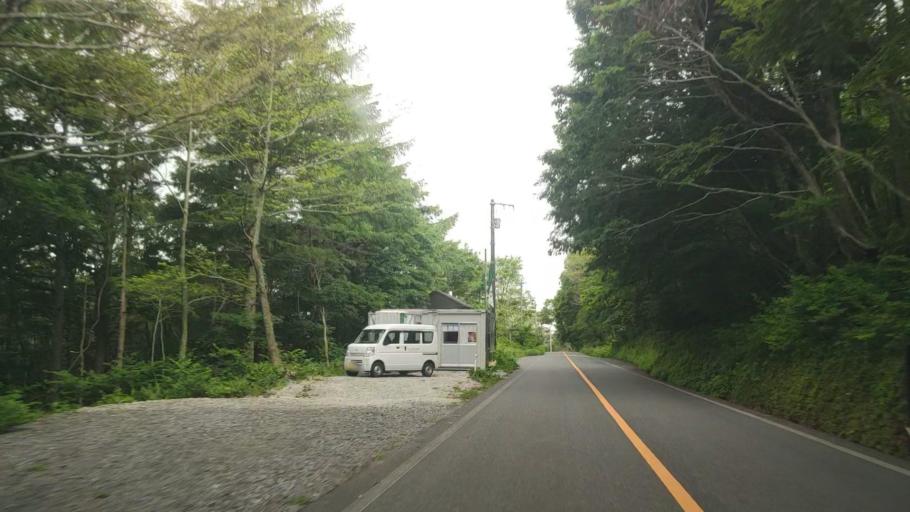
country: JP
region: Tottori
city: Yonago
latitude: 35.3601
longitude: 133.5273
